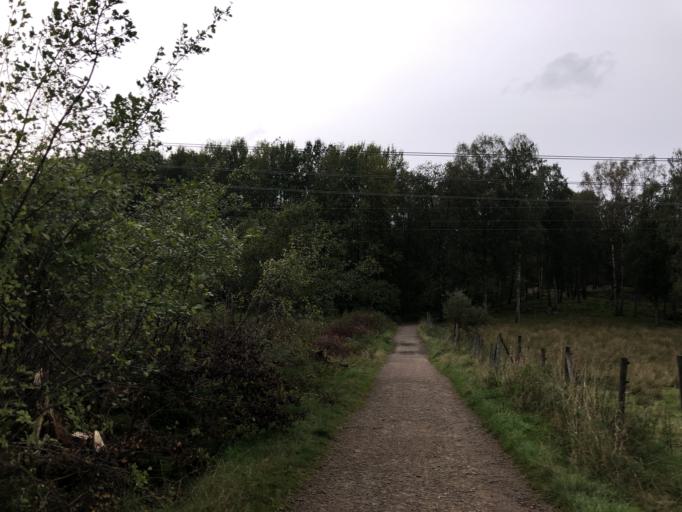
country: SE
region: Vaestra Goetaland
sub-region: Goteborg
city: Majorna
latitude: 57.7469
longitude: 11.9042
